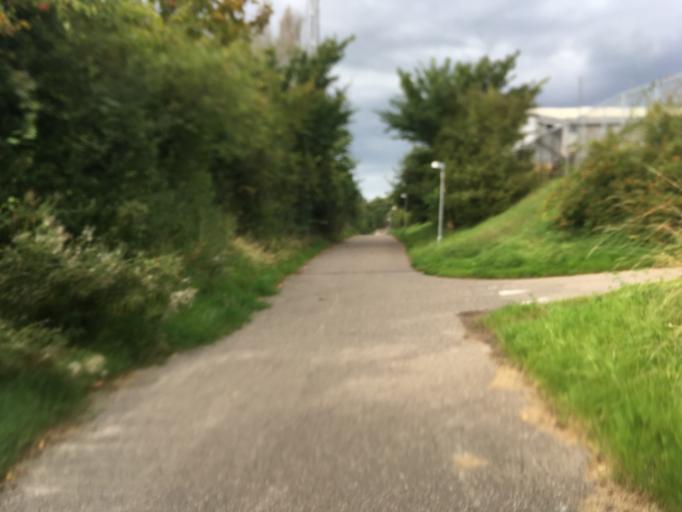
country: DK
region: Capital Region
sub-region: Hillerod Kommune
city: Hillerod
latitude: 55.9324
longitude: 12.2761
